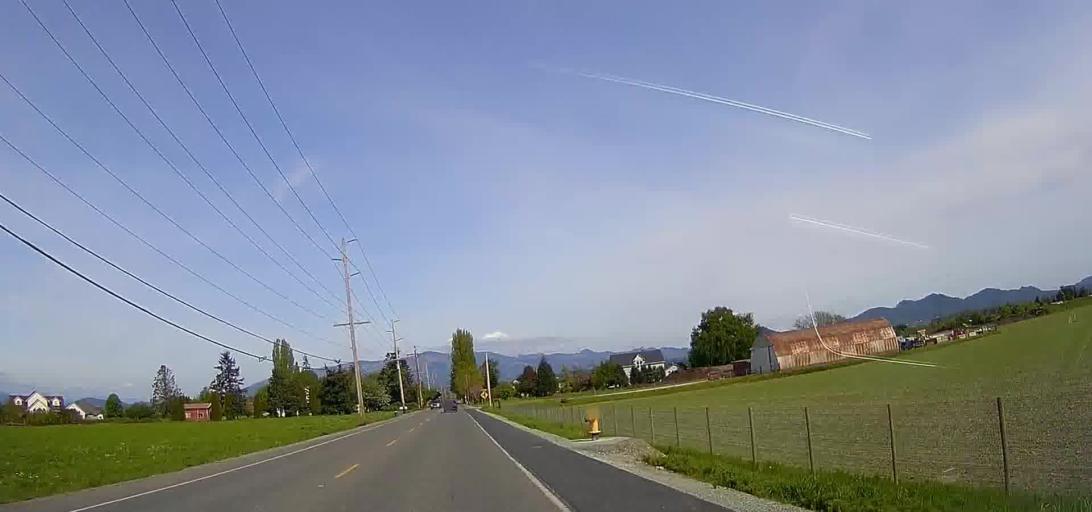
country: US
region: Washington
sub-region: Skagit County
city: Mount Vernon
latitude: 48.4209
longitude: -122.3929
